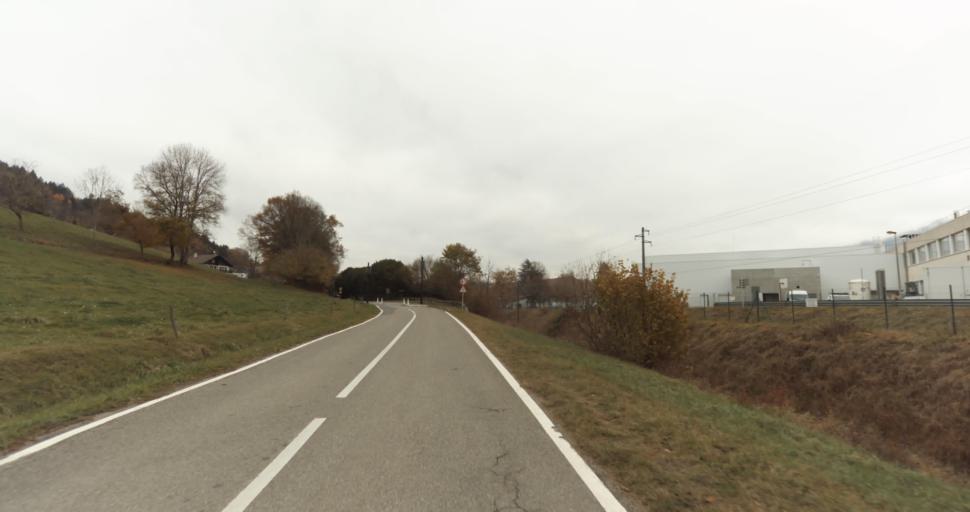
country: FR
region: Rhone-Alpes
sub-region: Departement de la Haute-Savoie
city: Saint-Martin-Bellevue
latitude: 45.9502
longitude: 6.1570
